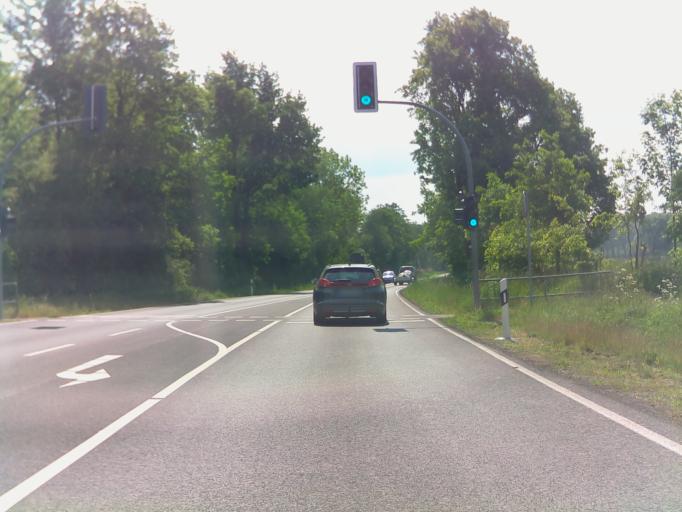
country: DE
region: Saxony-Anhalt
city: Luderitz
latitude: 52.5694
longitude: 11.7479
